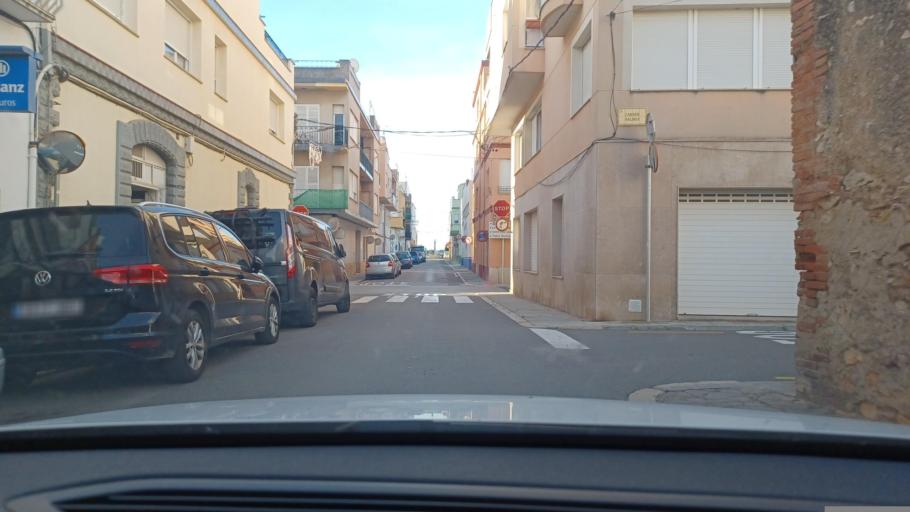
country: ES
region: Catalonia
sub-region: Provincia de Tarragona
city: Ulldecona
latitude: 40.5966
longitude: 0.4448
